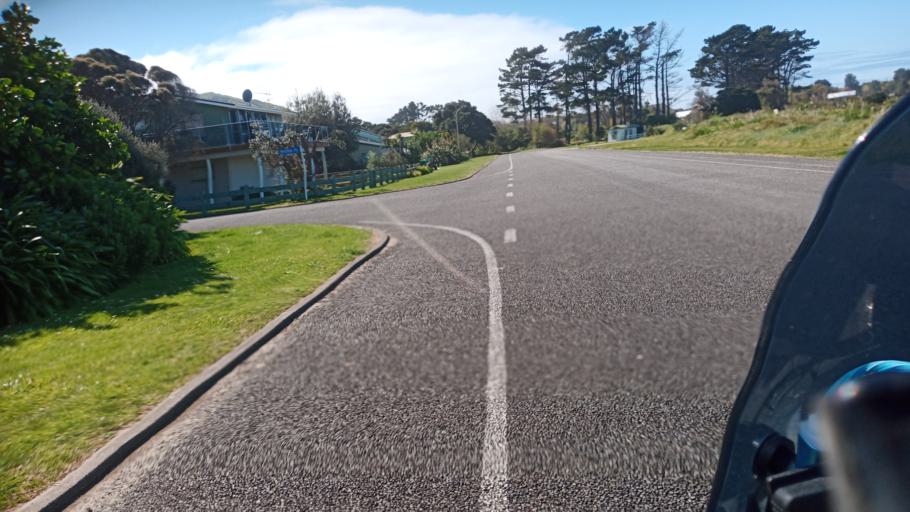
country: NZ
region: Gisborne
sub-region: Gisborne District
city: Gisborne
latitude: -39.0158
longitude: 177.8855
